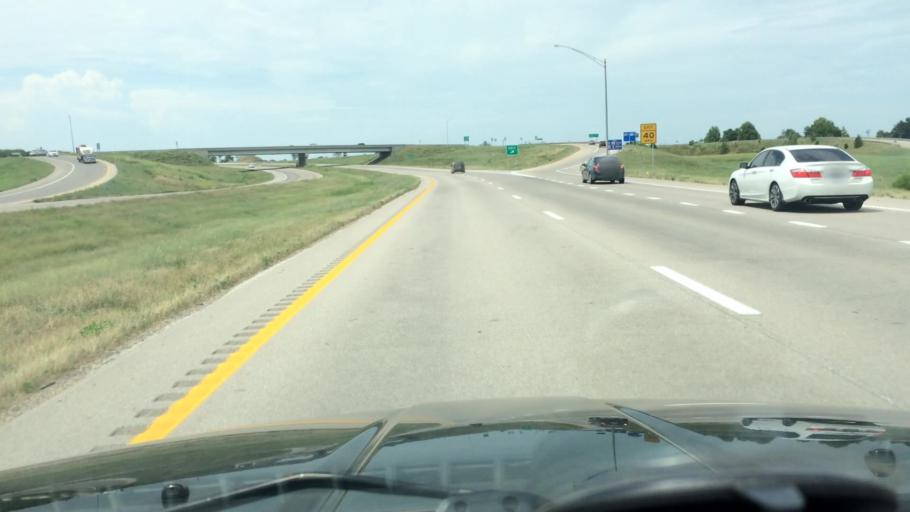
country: US
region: Missouri
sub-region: Polk County
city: Bolivar
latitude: 37.5722
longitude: -93.3968
